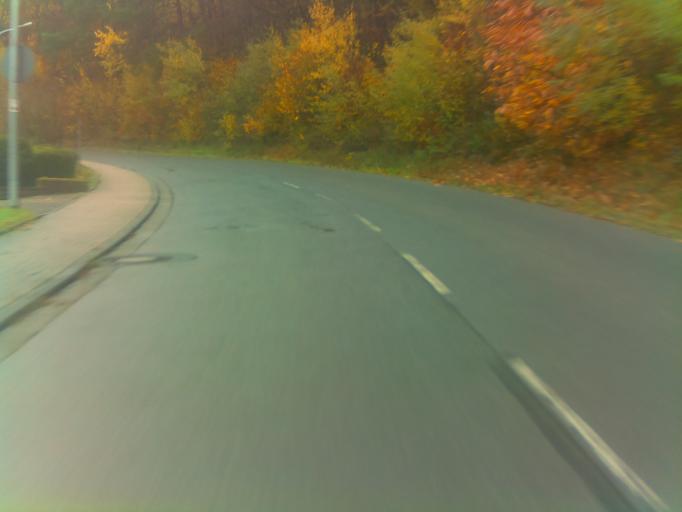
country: DE
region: Hesse
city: Neckarsteinach
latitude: 49.4065
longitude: 8.8456
